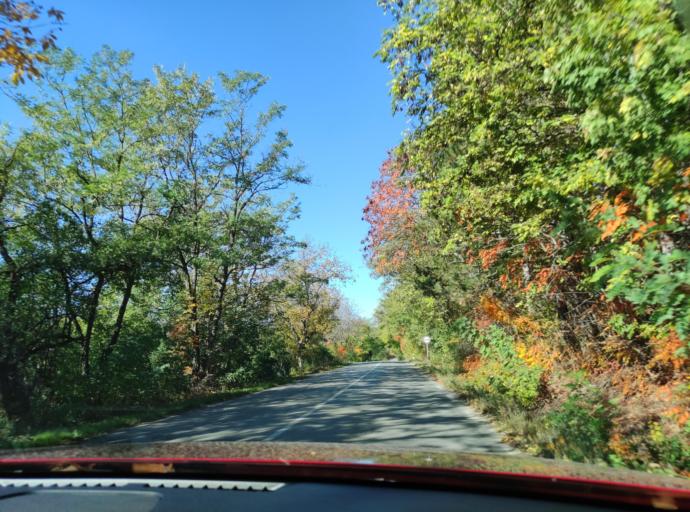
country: BG
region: Montana
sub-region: Obshtina Montana
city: Montana
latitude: 43.3990
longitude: 23.0953
